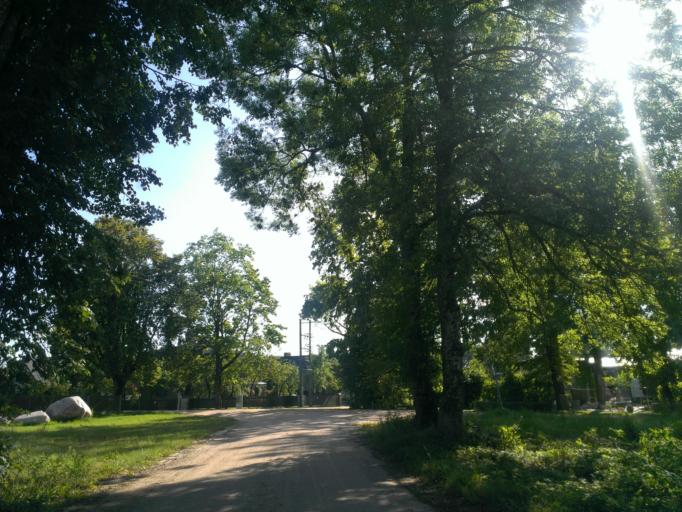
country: LV
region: Sigulda
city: Sigulda
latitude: 57.1652
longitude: 24.8863
